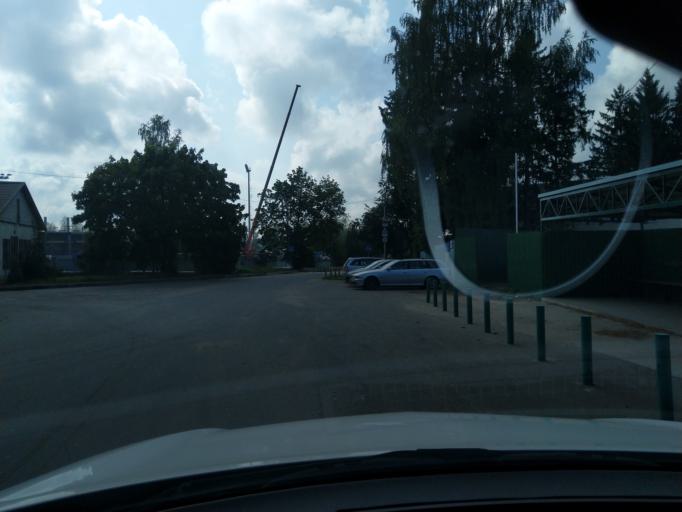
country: BY
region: Minsk
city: Zhdanovichy
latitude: 53.9061
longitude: 27.4136
